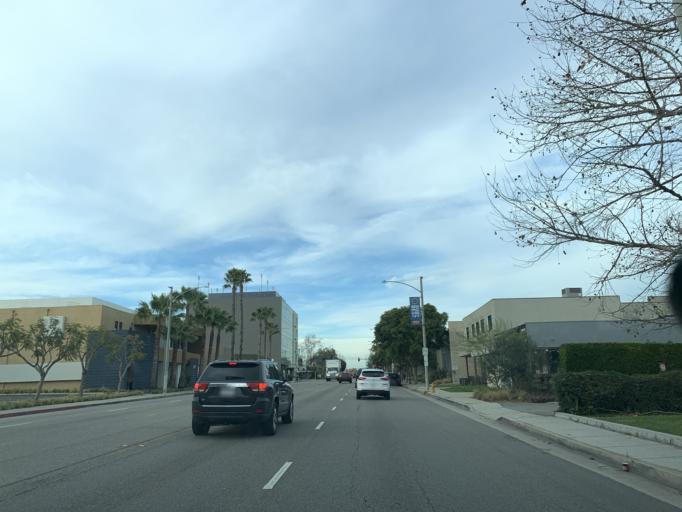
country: US
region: California
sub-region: Los Angeles County
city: Signal Hill
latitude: 33.8248
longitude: -118.1894
